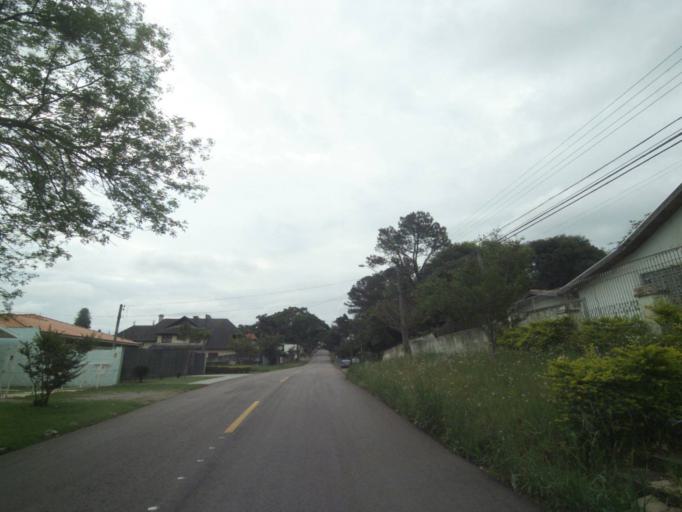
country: BR
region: Parana
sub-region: Curitiba
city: Curitiba
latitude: -25.4032
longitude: -49.2828
